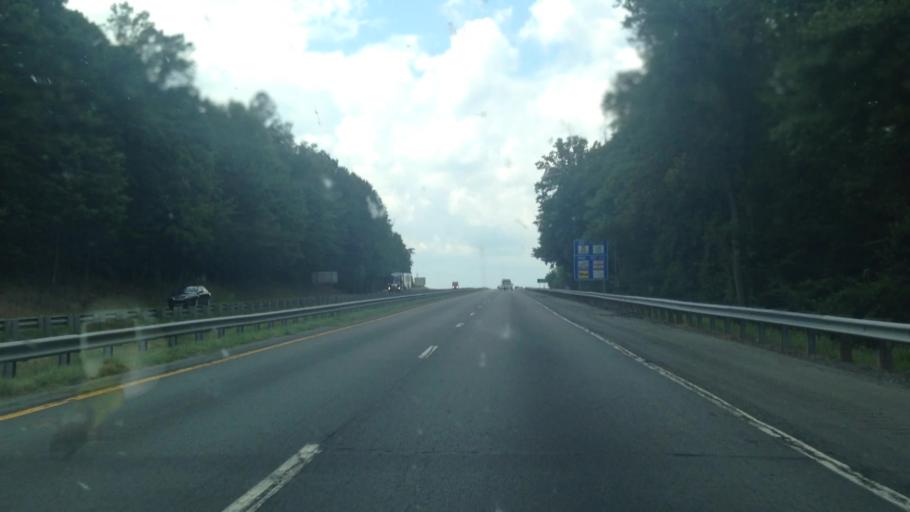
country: US
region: North Carolina
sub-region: Forsyth County
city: Tobaccoville
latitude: 36.2537
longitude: -80.3582
